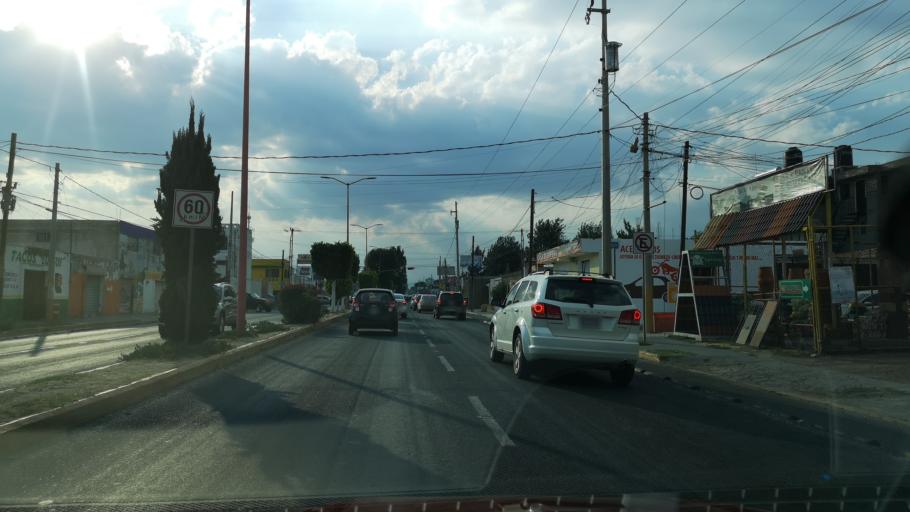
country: MX
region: Puebla
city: Cholula
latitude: 19.0683
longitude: -98.3083
